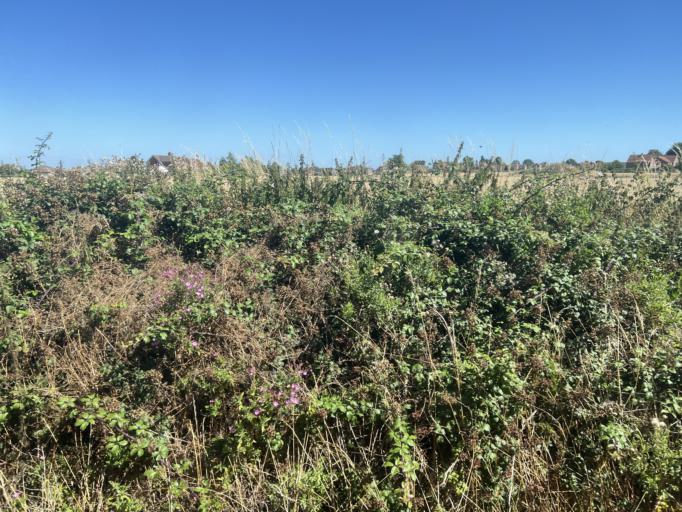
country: GB
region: England
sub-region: Lincolnshire
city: Wainfleet All Saints
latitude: 53.1079
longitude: 0.2288
